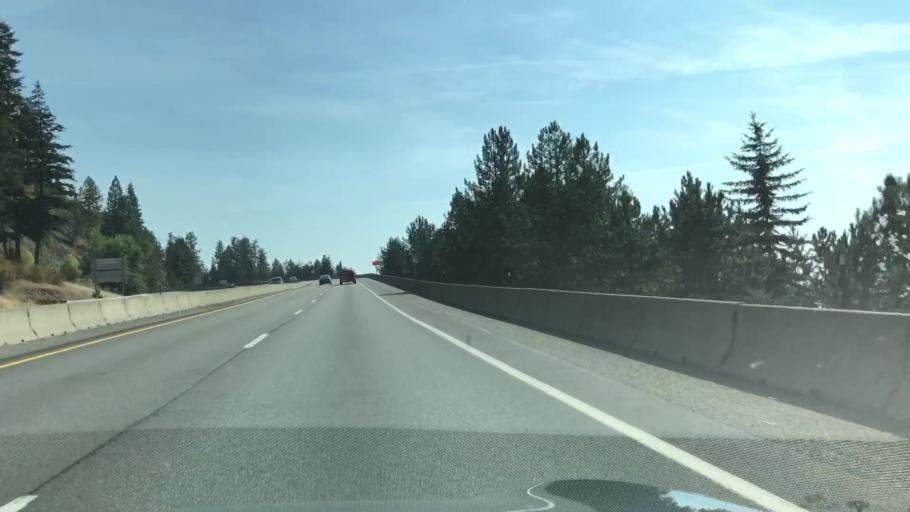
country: US
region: Idaho
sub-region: Kootenai County
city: Coeur d'Alene
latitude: 47.6677
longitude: -116.7508
